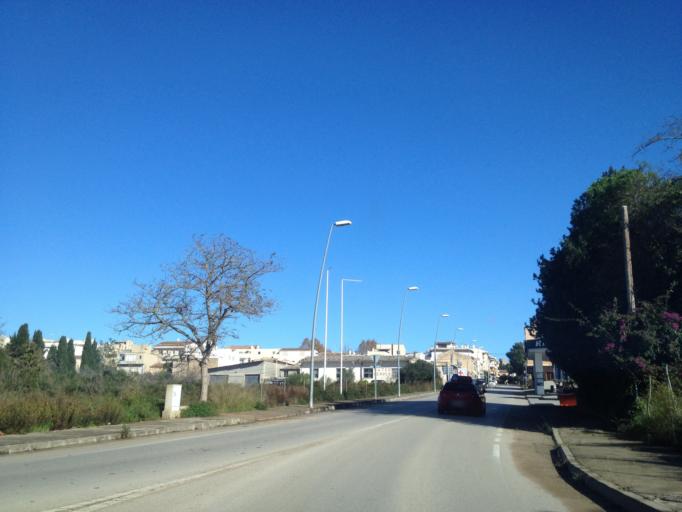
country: ES
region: Balearic Islands
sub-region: Illes Balears
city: Arta
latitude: 39.6892
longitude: 3.3462
